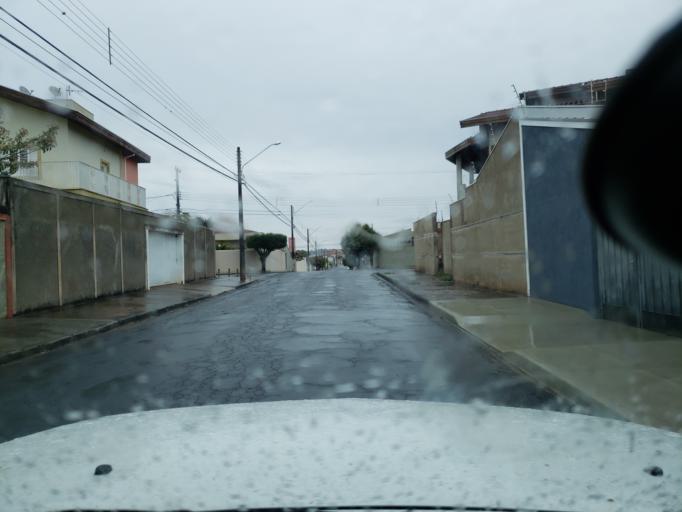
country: BR
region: Sao Paulo
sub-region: Moji-Guacu
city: Mogi-Gaucu
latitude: -22.3818
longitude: -46.9366
